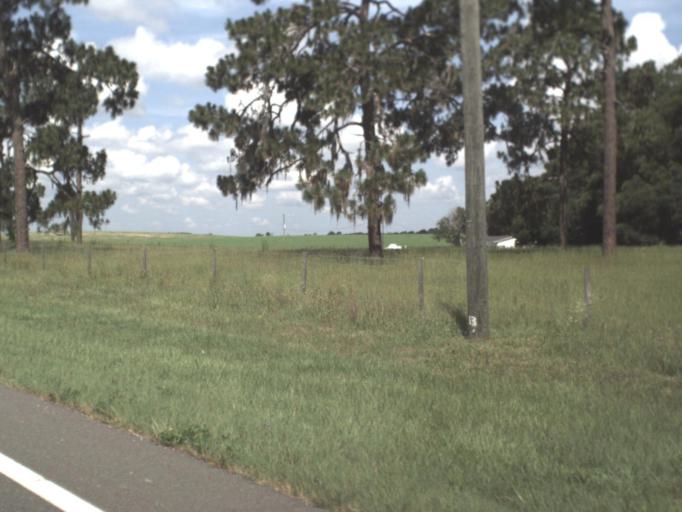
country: US
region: Florida
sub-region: Alachua County
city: Archer
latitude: 29.5225
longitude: -82.5405
